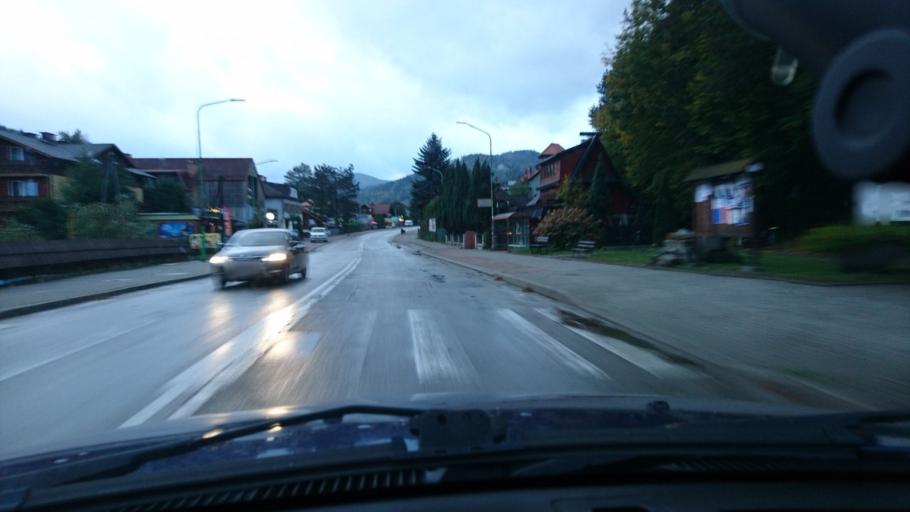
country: PL
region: Silesian Voivodeship
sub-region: Powiat bielski
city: Szczyrk
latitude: 49.7184
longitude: 19.0356
